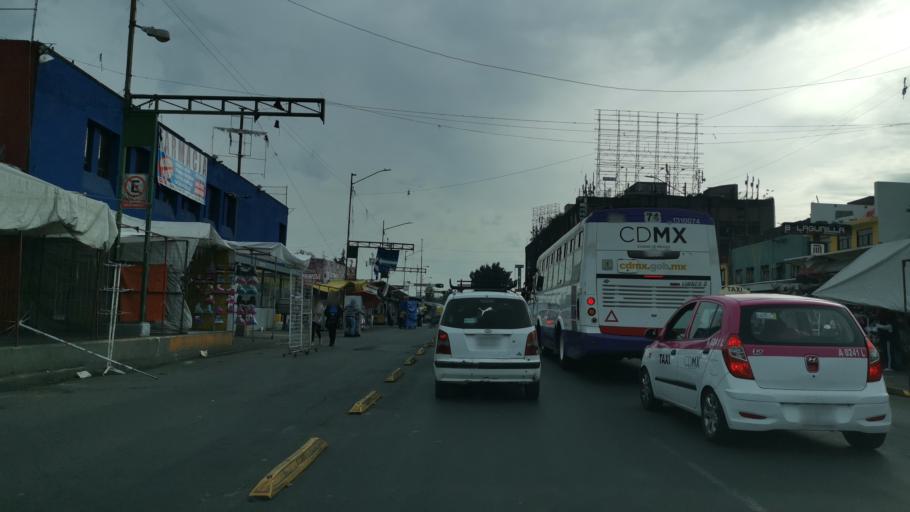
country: MX
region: Mexico City
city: Cuauhtemoc
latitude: 19.4433
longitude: -99.1318
